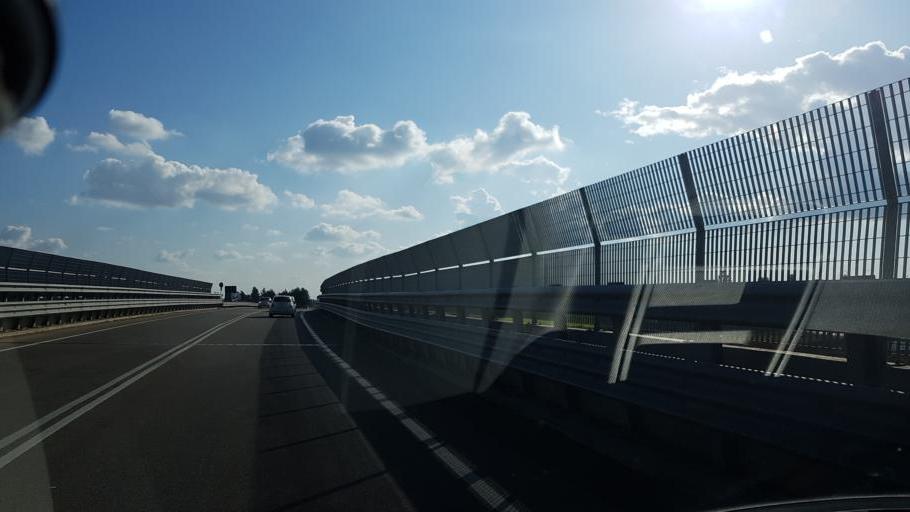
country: IT
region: Apulia
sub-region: Provincia di Lecce
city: Salice Salentino
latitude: 40.3886
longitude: 17.9694
